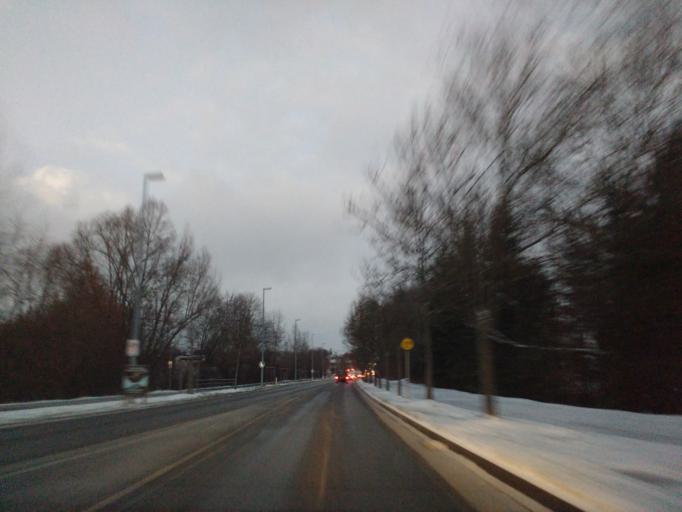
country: DE
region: Bavaria
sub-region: Swabia
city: Kempten (Allgaeu)
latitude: 47.7144
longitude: 10.2893
